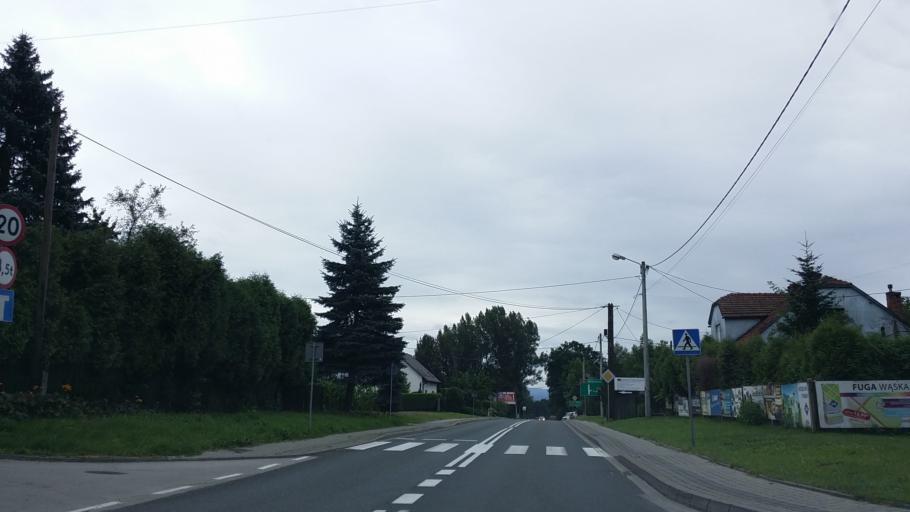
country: PL
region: Lesser Poland Voivodeship
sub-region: Powiat oswiecimski
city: Zator
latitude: 49.9910
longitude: 19.4382
